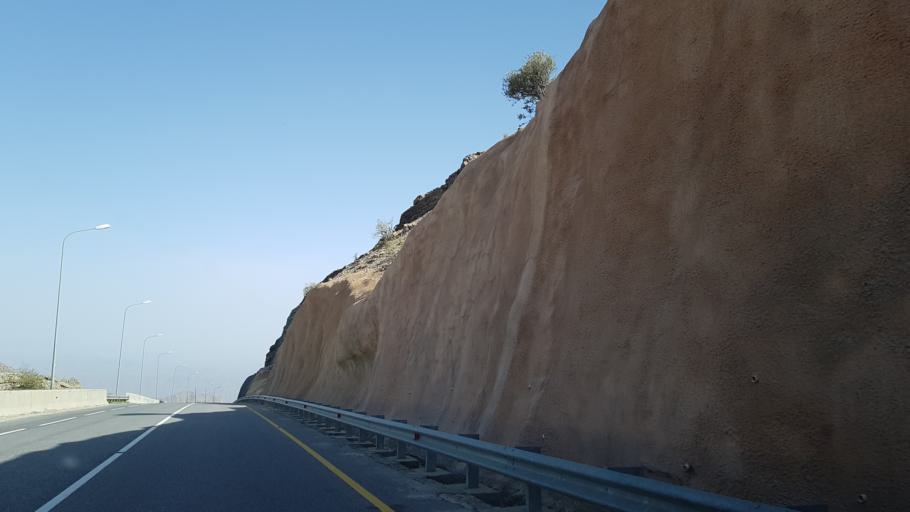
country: OM
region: Muhafazat ad Dakhiliyah
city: Izki
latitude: 23.0149
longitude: 57.6955
